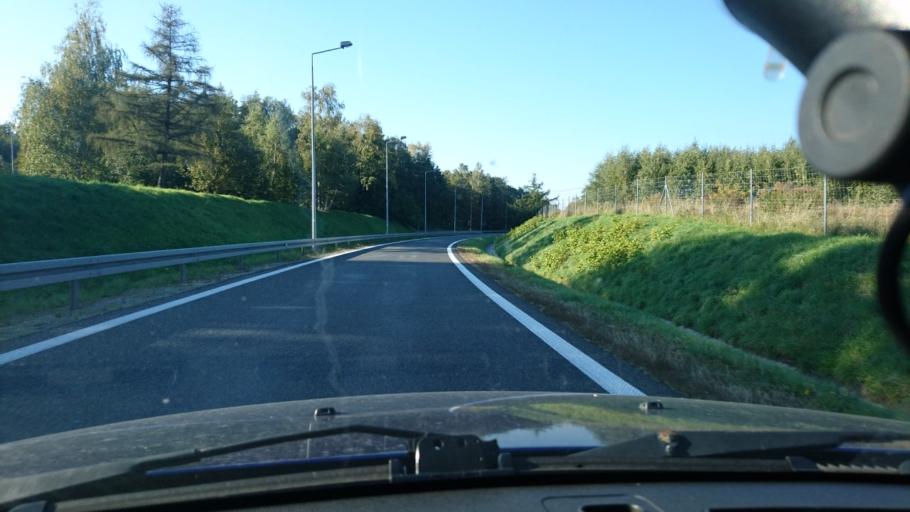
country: PL
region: Silesian Voivodeship
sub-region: Bielsko-Biala
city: Bielsko-Biala
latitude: 49.8503
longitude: 19.0305
